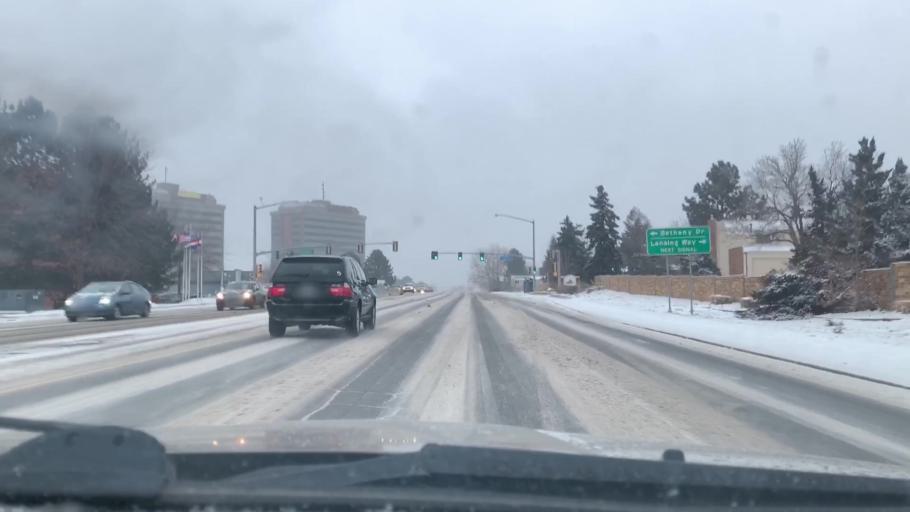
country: US
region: Colorado
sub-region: Adams County
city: Aurora
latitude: 39.6625
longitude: -104.8573
